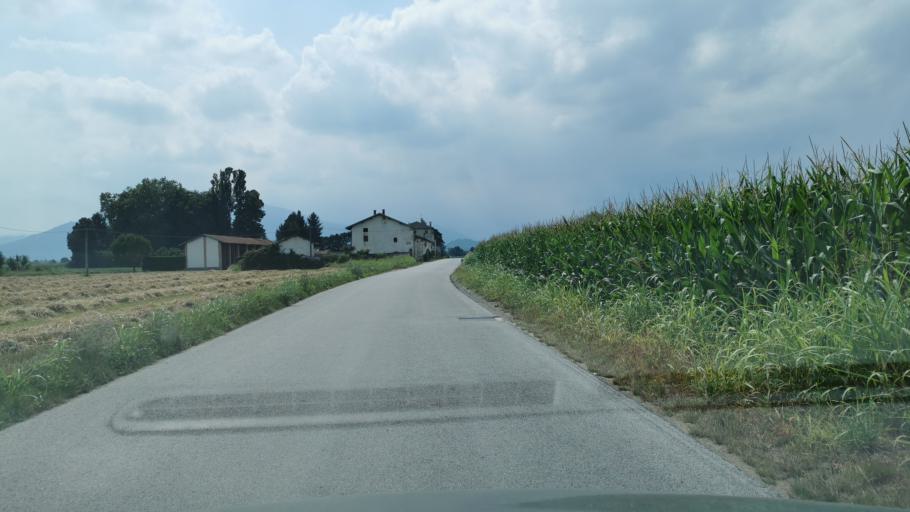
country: IT
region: Piedmont
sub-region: Provincia di Cuneo
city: San Rocco
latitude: 44.4304
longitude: 7.4846
